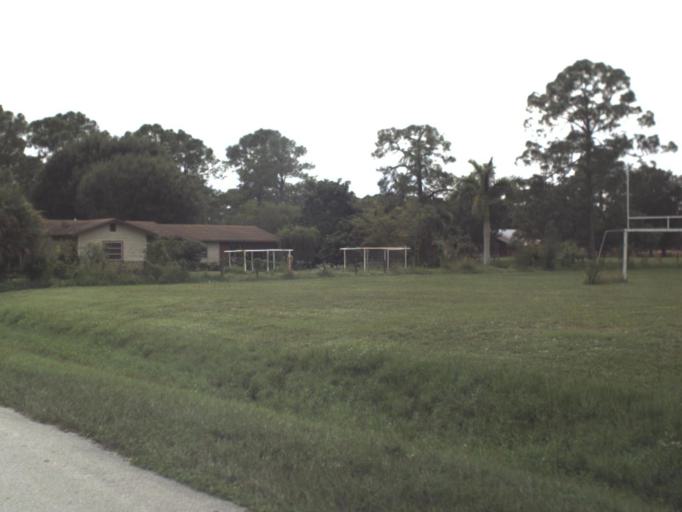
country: US
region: Florida
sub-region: Lee County
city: Fort Myers Shores
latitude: 26.7371
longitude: -81.7611
